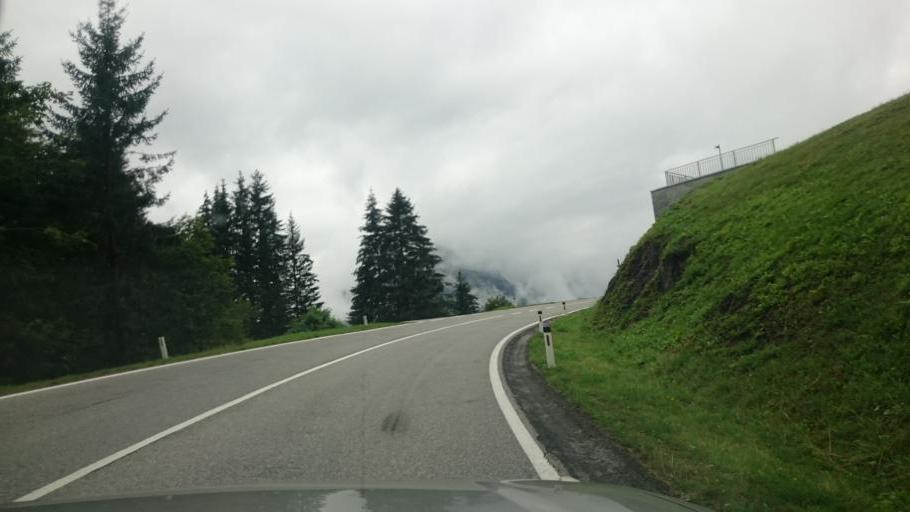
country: AT
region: Vorarlberg
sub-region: Politischer Bezirk Bregenz
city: Schroecken
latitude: 47.2595
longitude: 10.0951
